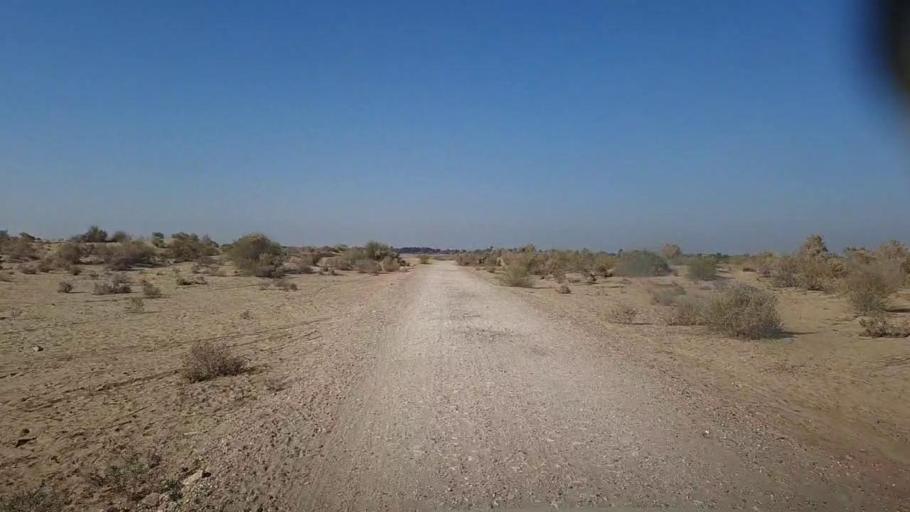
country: PK
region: Sindh
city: Khairpur
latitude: 27.9611
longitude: 69.8120
